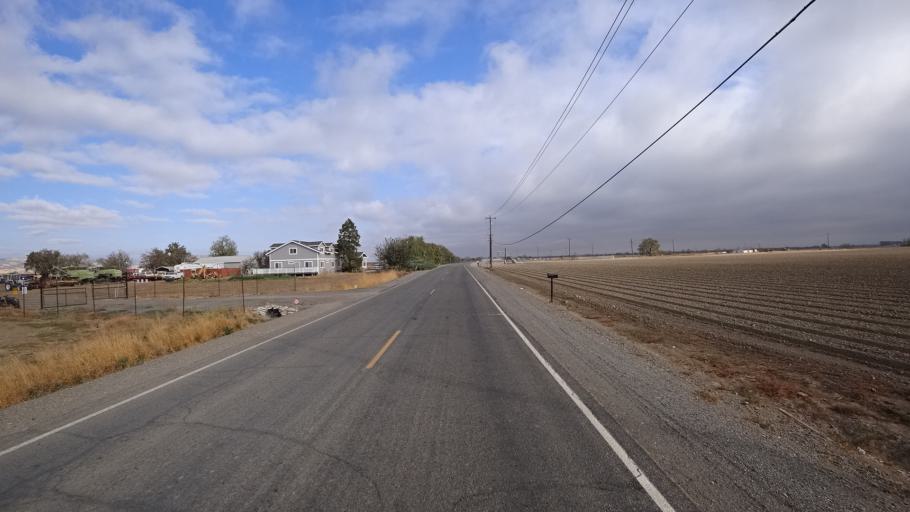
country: US
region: California
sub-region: Yolo County
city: Esparto
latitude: 38.7077
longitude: -122.0132
